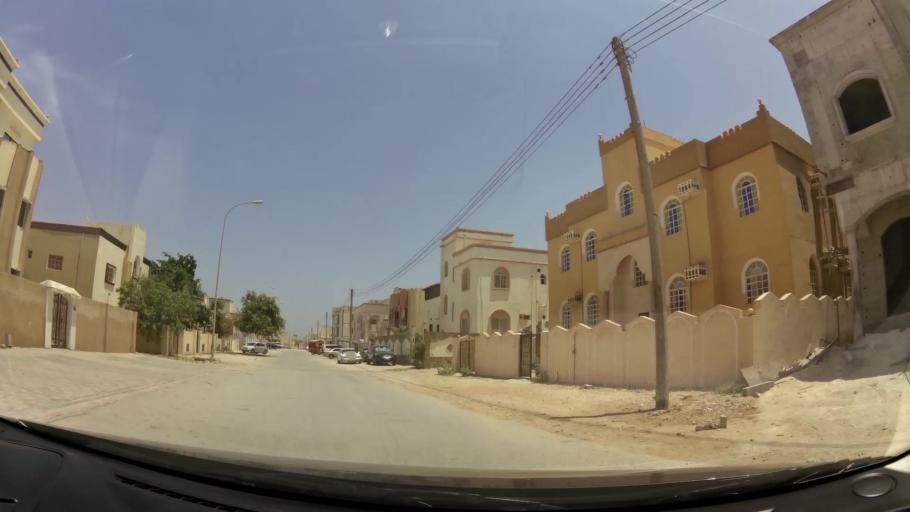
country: OM
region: Zufar
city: Salalah
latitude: 17.0726
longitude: 54.1489
